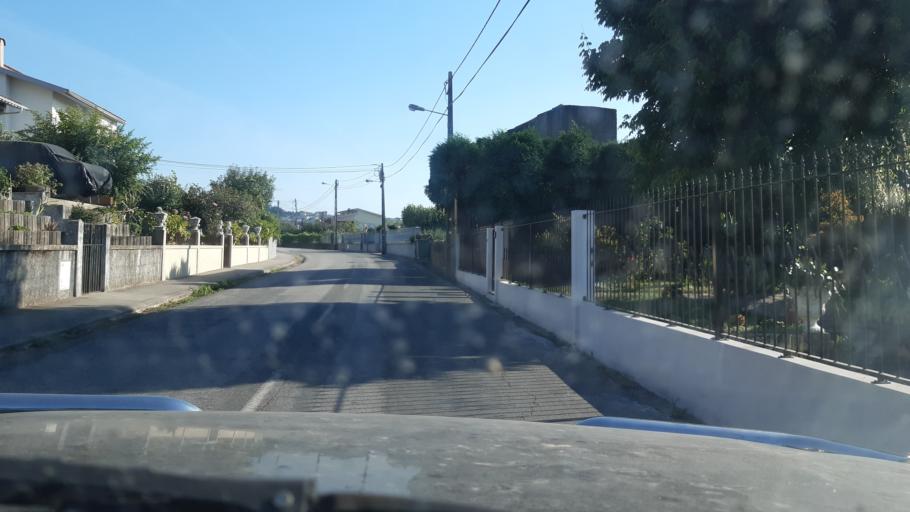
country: PT
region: Aveiro
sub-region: Agueda
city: Agueda
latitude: 40.5676
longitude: -8.4335
